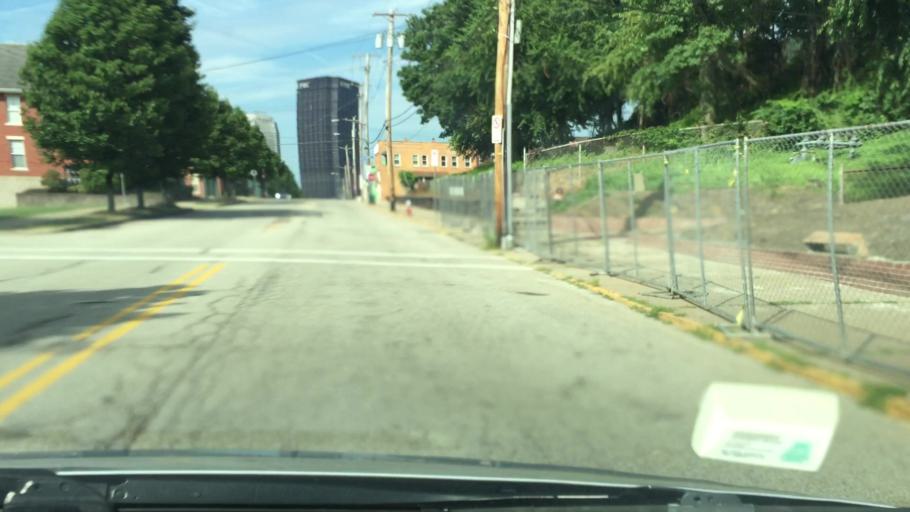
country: US
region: Pennsylvania
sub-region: Allegheny County
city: Pittsburgh
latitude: 40.4452
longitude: -79.9858
